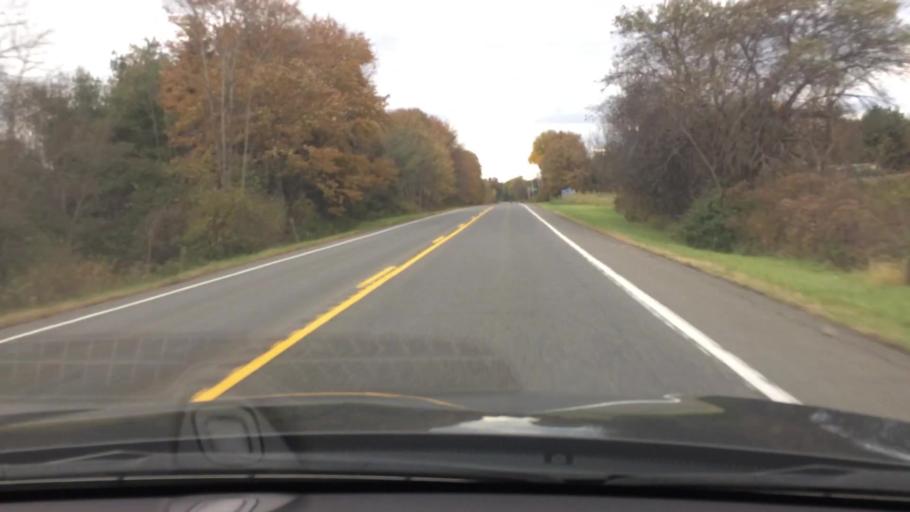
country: US
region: New York
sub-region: Columbia County
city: Kinderhook
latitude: 42.3378
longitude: -73.7046
